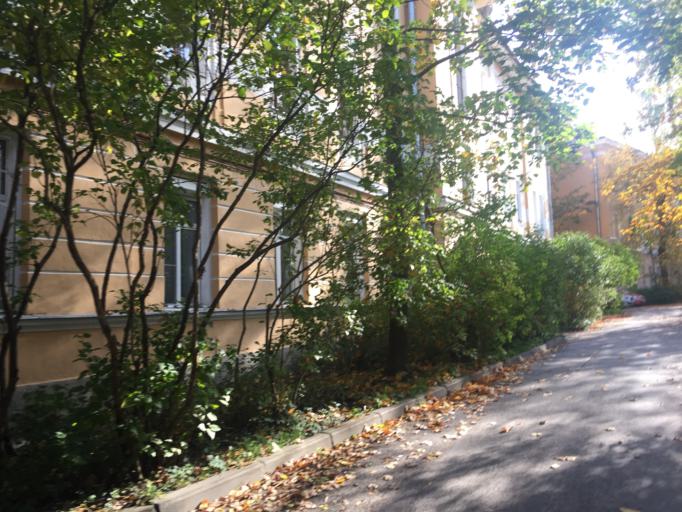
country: RU
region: St.-Petersburg
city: Pushkin
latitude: 59.7244
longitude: 30.3986
